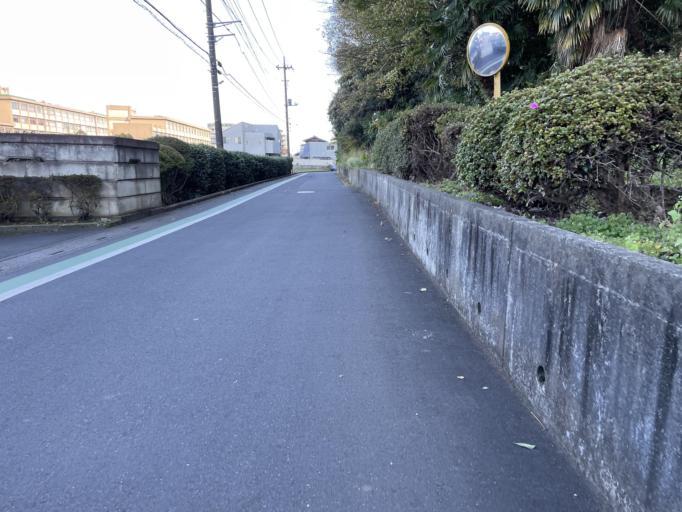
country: JP
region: Saitama
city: Wako
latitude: 35.7966
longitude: 139.6259
